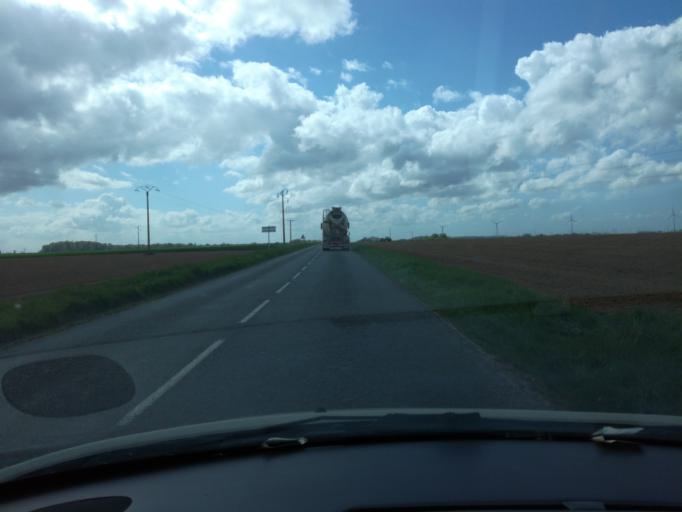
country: FR
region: Picardie
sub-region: Departement de la Somme
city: Picquigny
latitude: 49.8911
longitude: 2.1491
